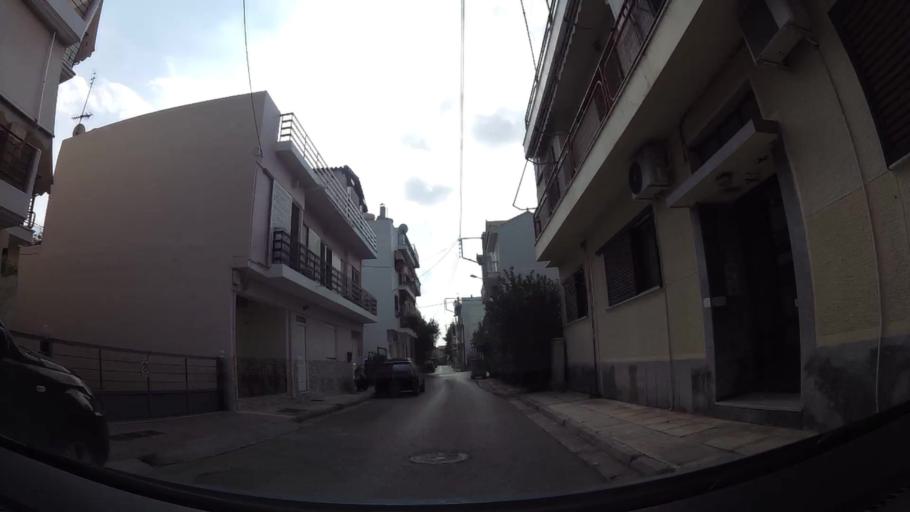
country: GR
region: Attica
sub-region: Nomarchia Athinas
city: Ilion
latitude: 38.0421
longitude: 23.7009
